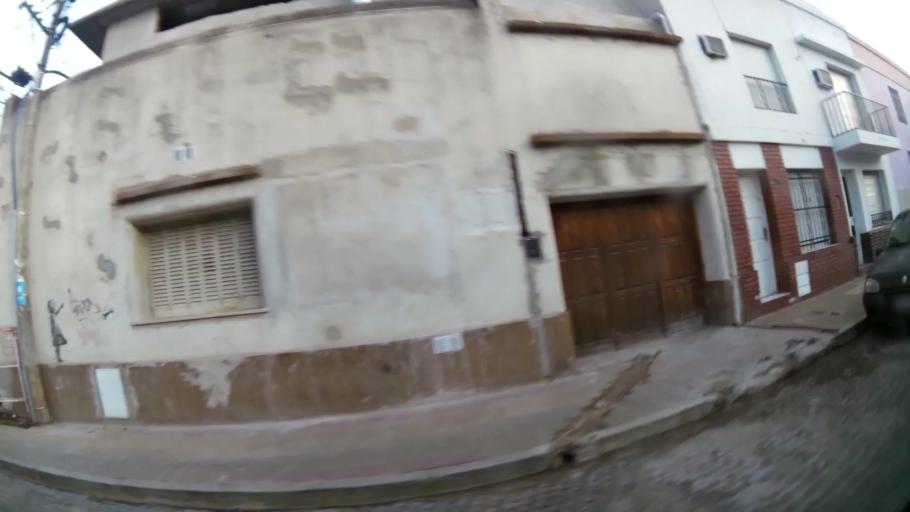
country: AR
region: Buenos Aires
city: San Nicolas de los Arroyos
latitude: -33.3290
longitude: -60.2212
